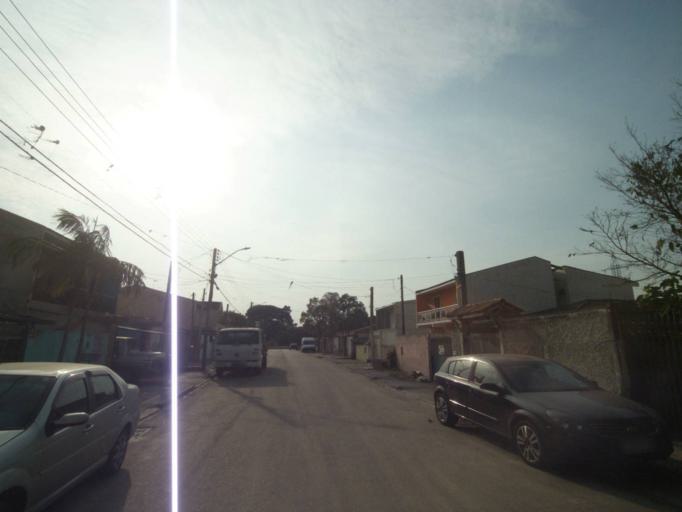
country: BR
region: Parana
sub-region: Sao Jose Dos Pinhais
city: Sao Jose dos Pinhais
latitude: -25.4955
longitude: -49.2054
